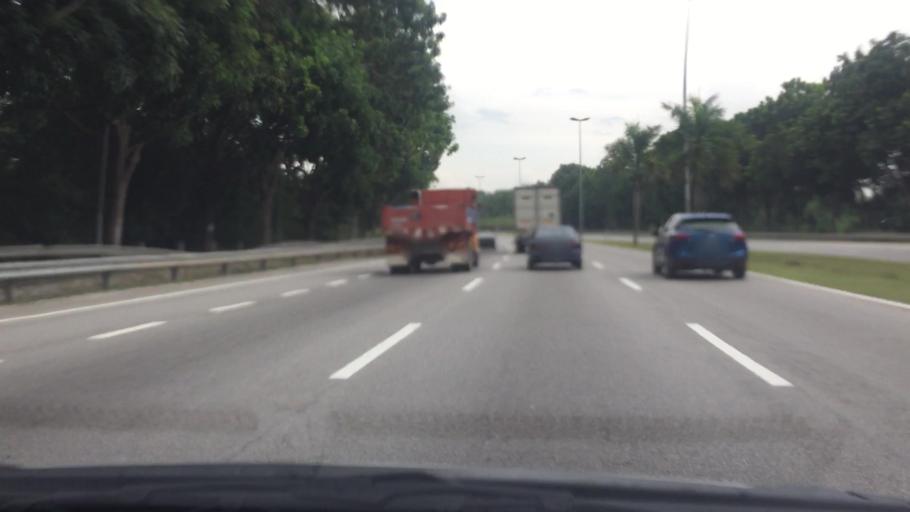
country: MY
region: Putrajaya
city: Putrajaya
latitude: 2.9062
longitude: 101.6588
